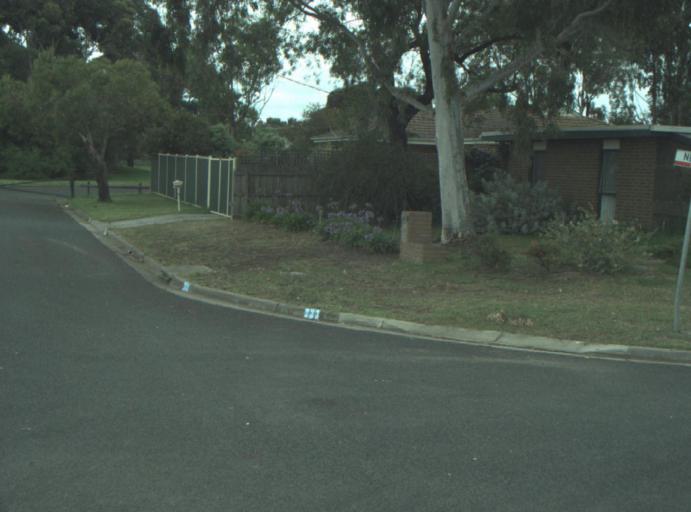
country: AU
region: Victoria
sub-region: Greater Geelong
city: Breakwater
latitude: -38.2017
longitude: 144.3410
